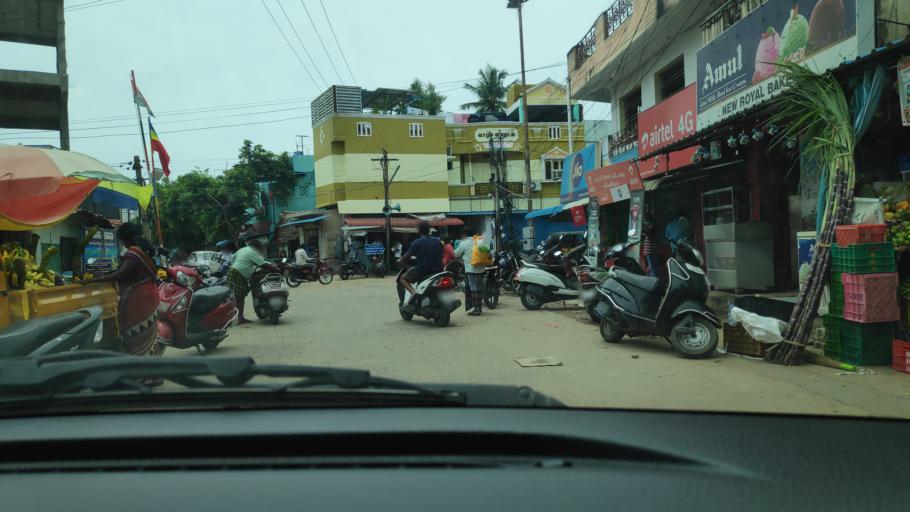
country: IN
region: Tamil Nadu
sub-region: Kancheepuram
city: Pallavaram
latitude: 12.9287
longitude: 80.1299
